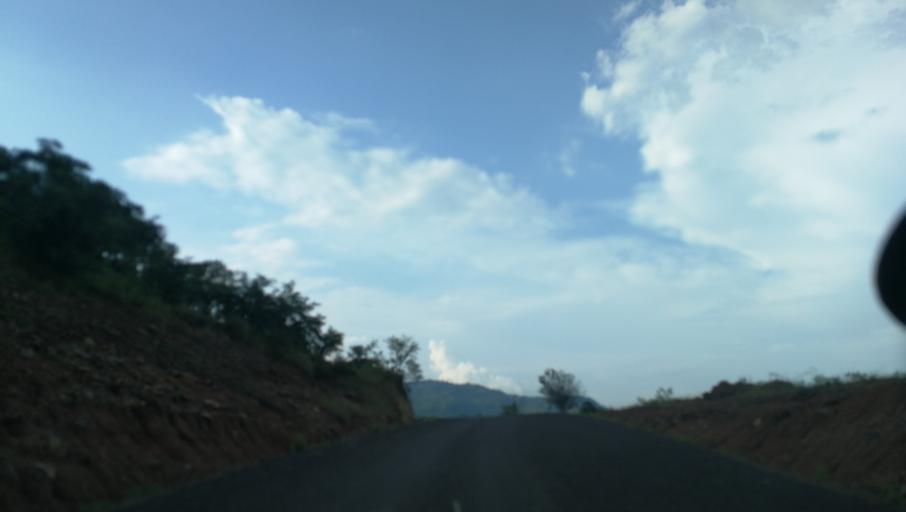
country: ET
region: Southern Nations, Nationalities, and People's Region
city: Areka
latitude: 6.8491
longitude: 37.2700
